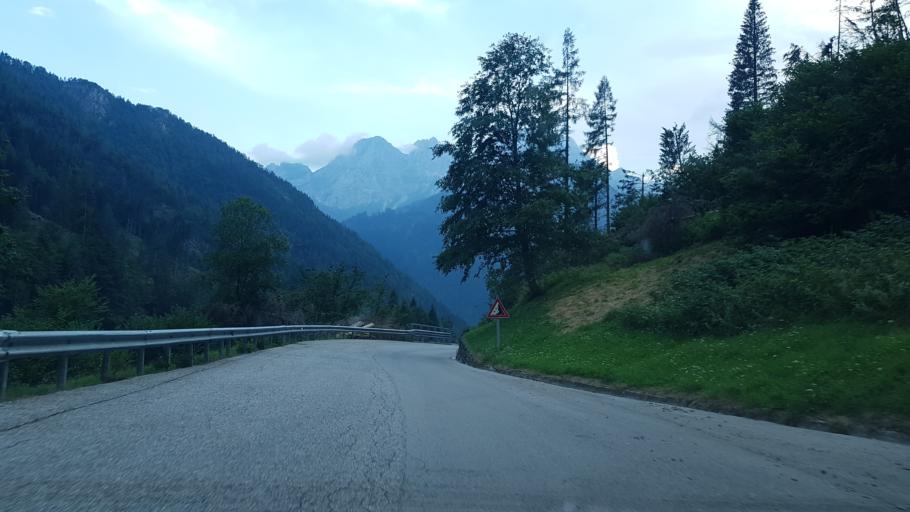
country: IT
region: Friuli Venezia Giulia
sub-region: Provincia di Udine
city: Forni Avoltri
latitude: 46.6040
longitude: 12.7786
